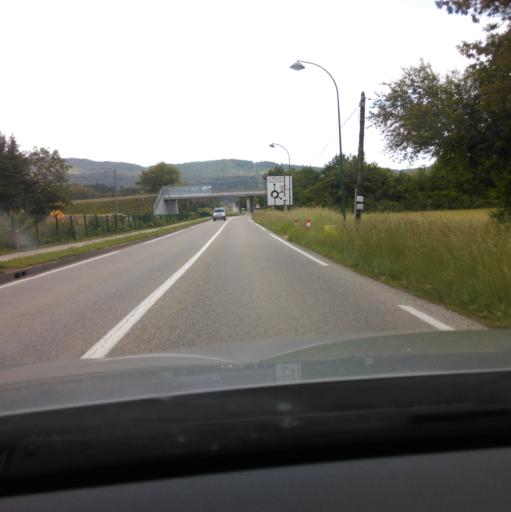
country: FR
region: Rhone-Alpes
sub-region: Departement de l'Ain
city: Montreal-la-Cluse
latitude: 46.1784
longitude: 5.5524
